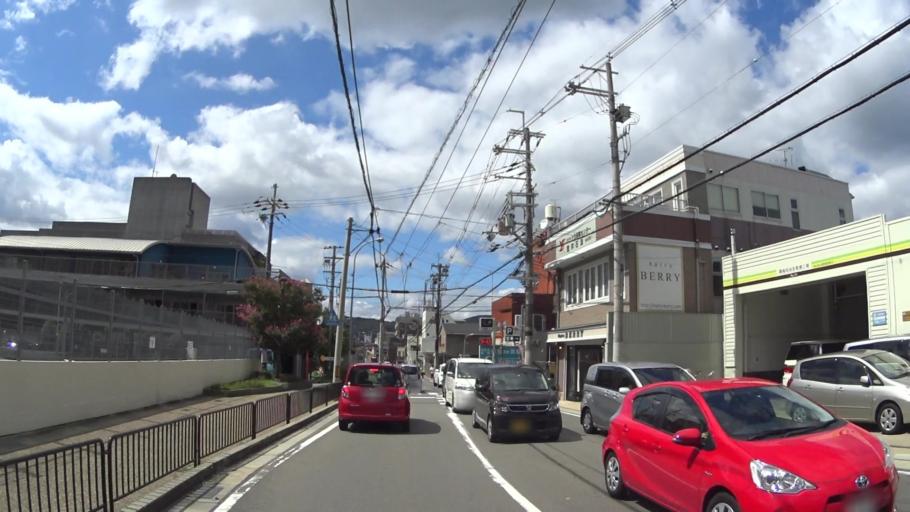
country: JP
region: Shiga Prefecture
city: Otsu-shi
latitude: 34.9868
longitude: 135.8172
